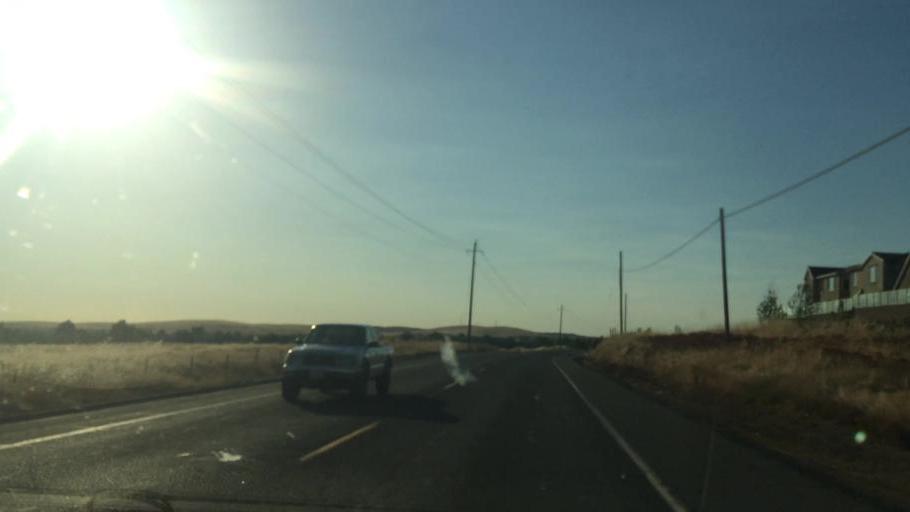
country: US
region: California
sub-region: El Dorado County
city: El Dorado Hills
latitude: 38.6164
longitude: -121.0483
